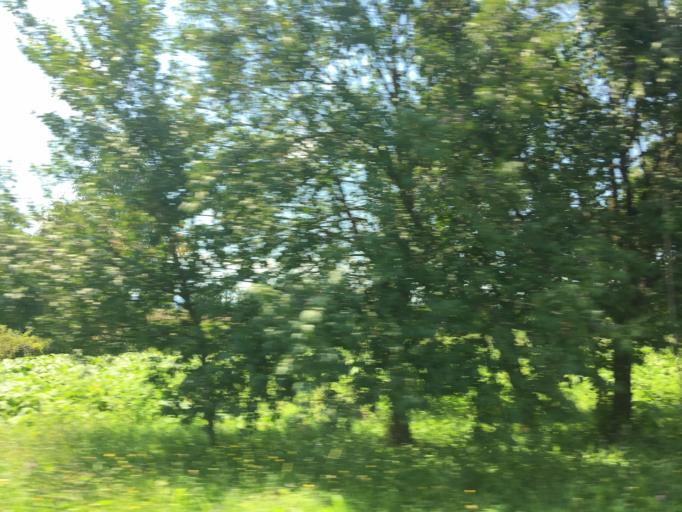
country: SI
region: Metlika
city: Metlika
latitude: 45.6228
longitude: 15.3209
